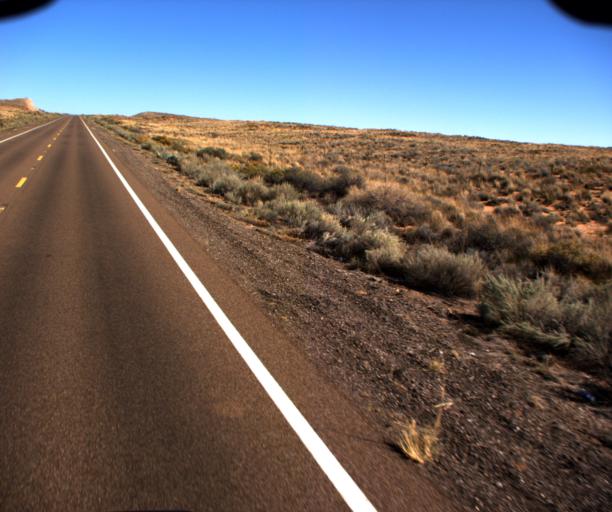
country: US
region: Arizona
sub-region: Navajo County
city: Winslow
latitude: 35.0633
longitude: -110.5812
